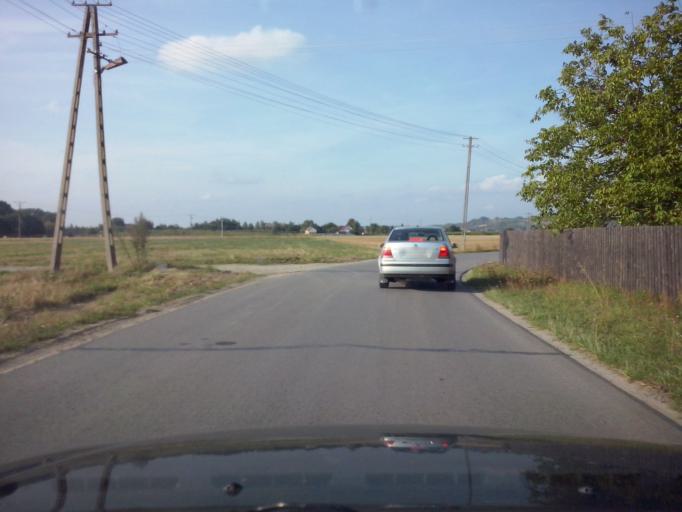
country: PL
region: Subcarpathian Voivodeship
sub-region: Powiat nizanski
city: Krzeszow
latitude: 50.3806
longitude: 22.3245
